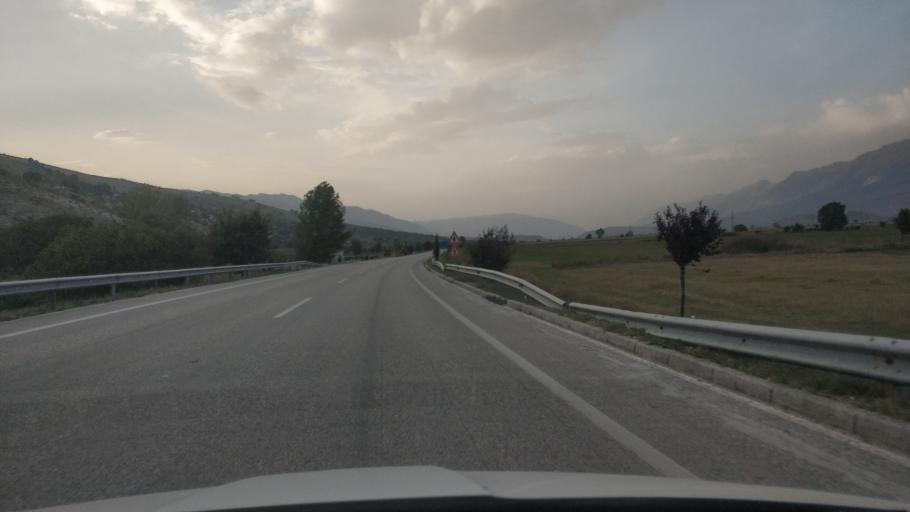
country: AL
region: Gjirokaster
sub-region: Rrethi i Gjirokastres
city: Libohove
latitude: 39.9789
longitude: 20.2310
